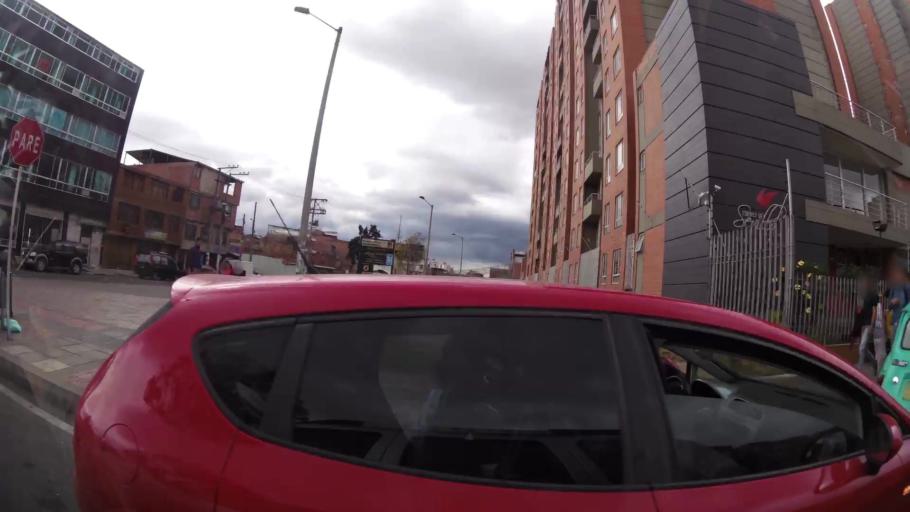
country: CO
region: Bogota D.C.
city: Bogota
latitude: 4.5976
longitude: -74.1411
